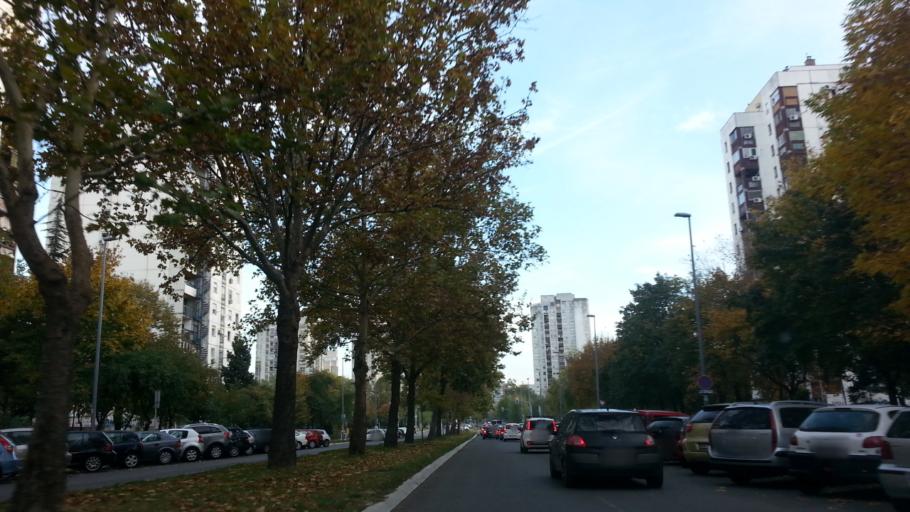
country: RS
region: Central Serbia
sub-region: Belgrade
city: Zemun
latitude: 44.8090
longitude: 20.3837
